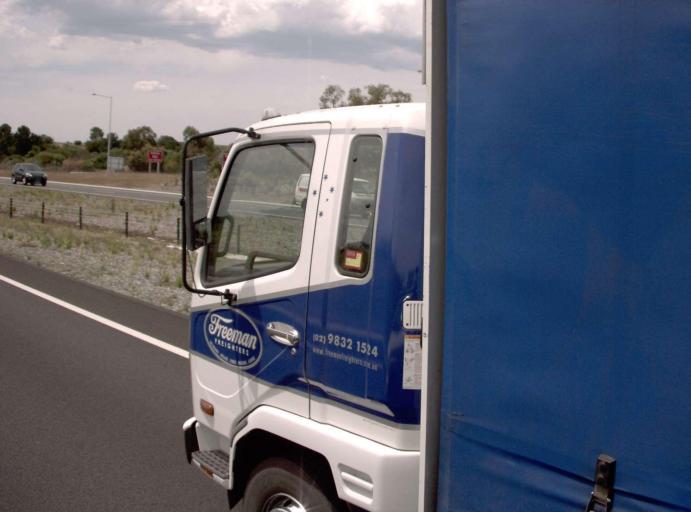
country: AU
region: Victoria
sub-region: Frankston
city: Langwarrin
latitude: -38.1401
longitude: 145.1730
